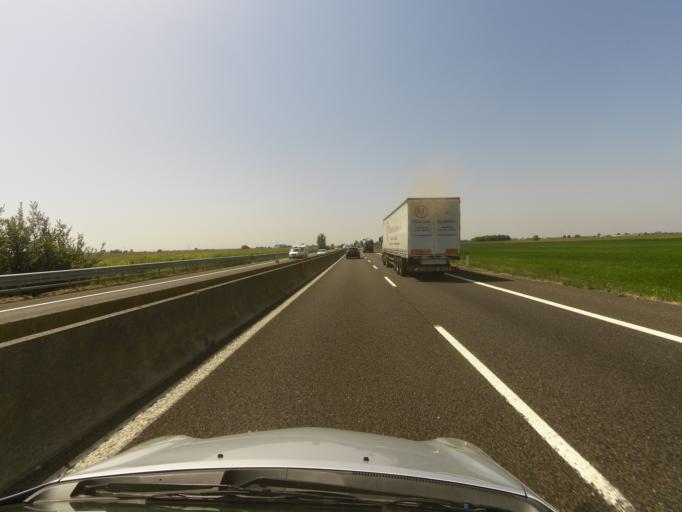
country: IT
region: Veneto
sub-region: Provincia di Rovigo
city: Fiesso Umbertiano
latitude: 44.9574
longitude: 11.6415
